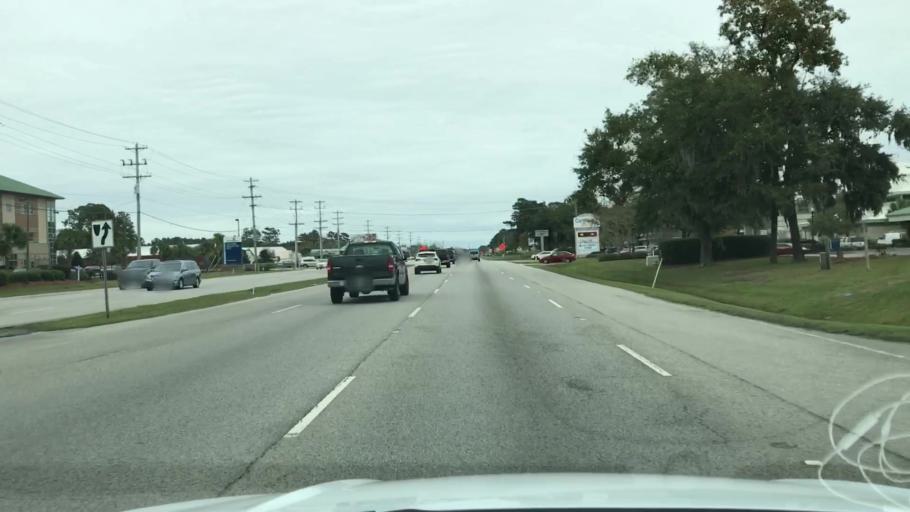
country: US
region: South Carolina
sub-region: Georgetown County
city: Murrells Inlet
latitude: 33.5600
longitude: -79.0408
